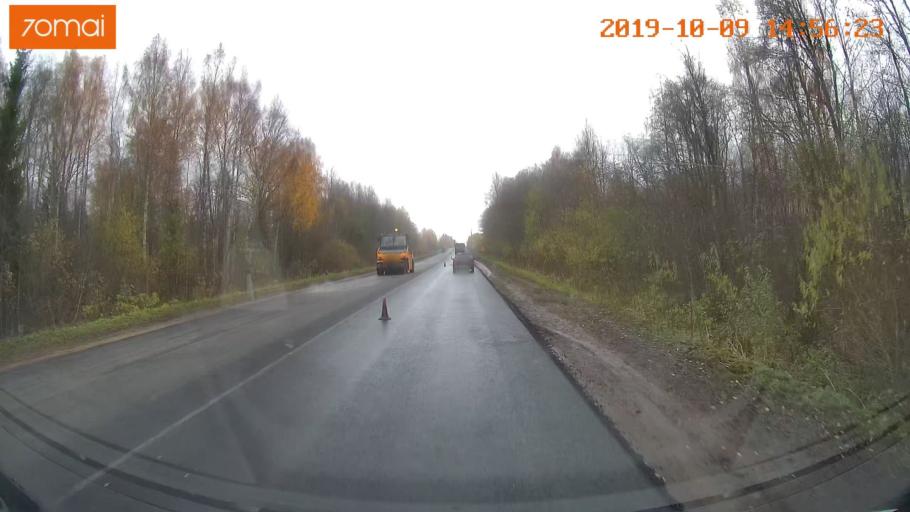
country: RU
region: Kostroma
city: Chistyye Bory
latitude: 58.3462
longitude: 41.6472
